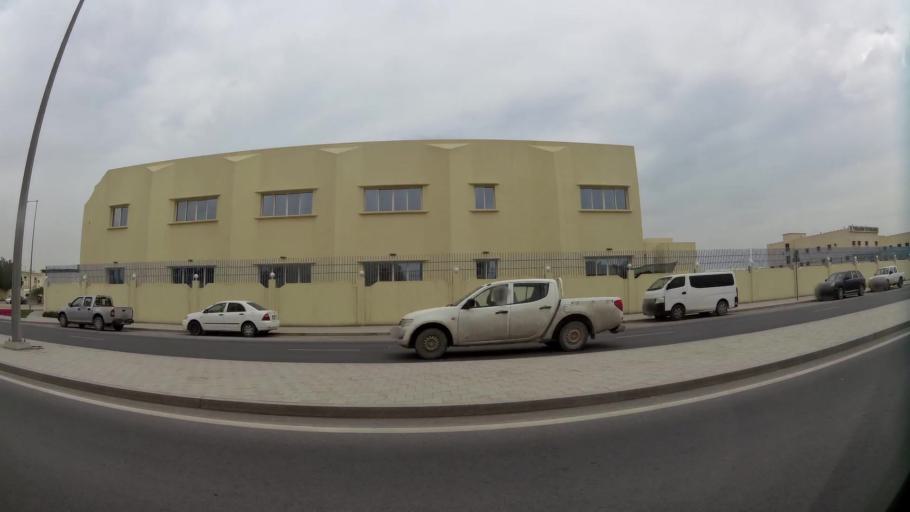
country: QA
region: Baladiyat ar Rayyan
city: Ar Rayyan
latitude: 25.2413
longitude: 51.4656
